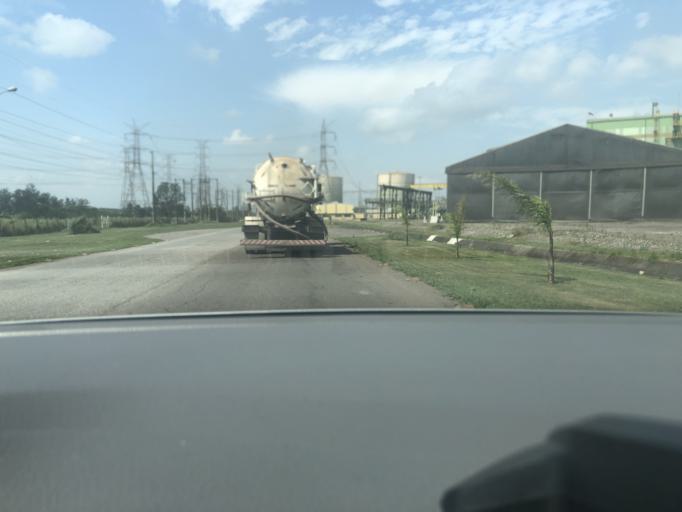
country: BR
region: Rio de Janeiro
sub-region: Itaguai
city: Itaguai
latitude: -22.9121
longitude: -43.7473
